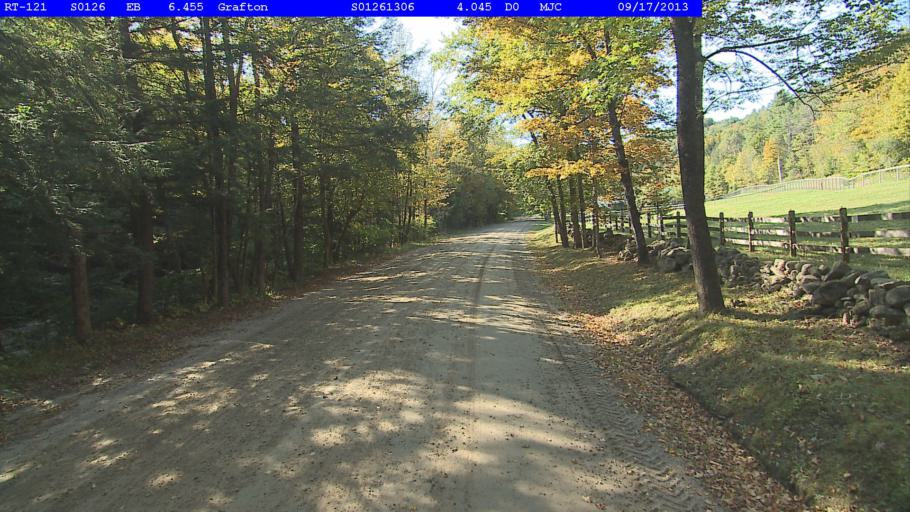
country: US
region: Vermont
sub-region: Windsor County
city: Chester
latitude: 43.1913
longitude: -72.6168
